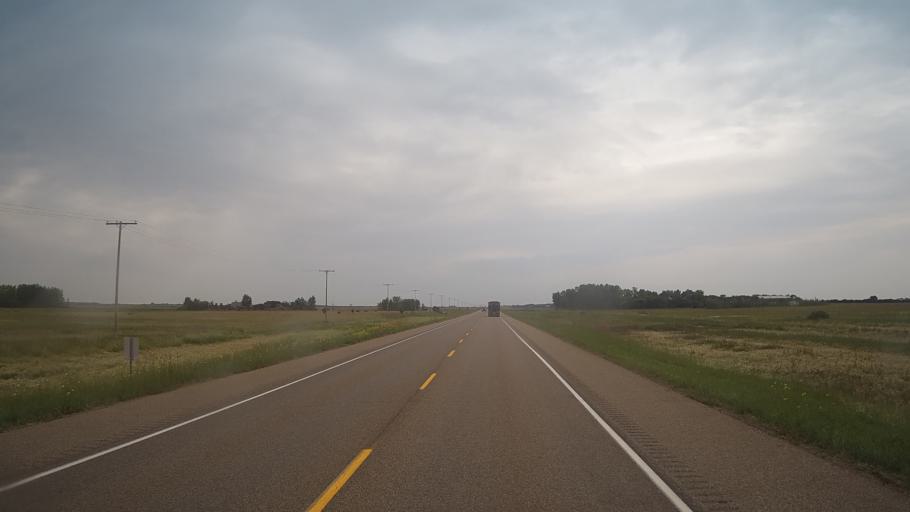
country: CA
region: Saskatchewan
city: Langham
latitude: 52.1289
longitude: -107.1354
